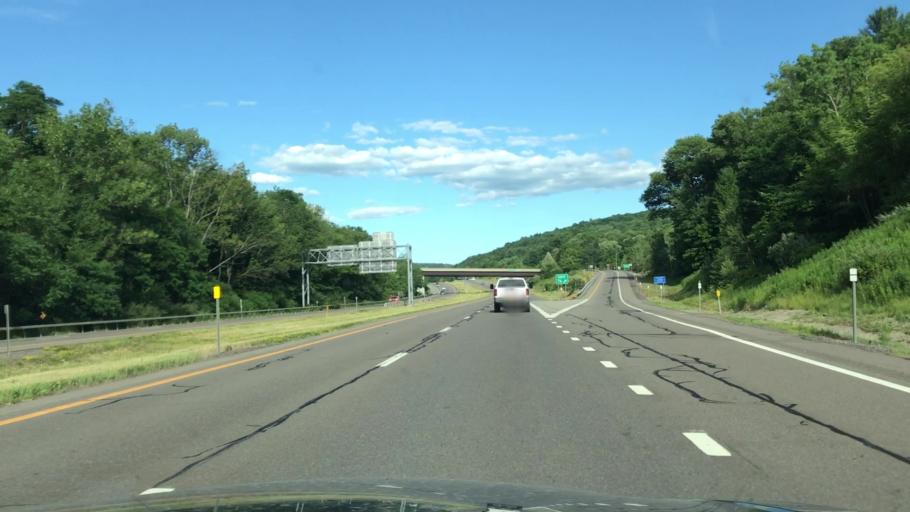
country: US
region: New York
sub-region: Broome County
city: Chenango Bridge
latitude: 42.1006
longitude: -75.7987
